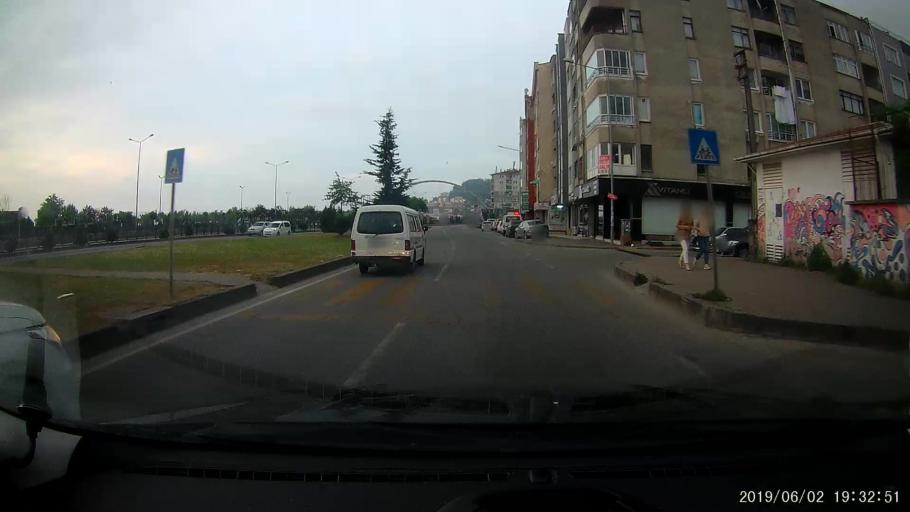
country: TR
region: Giresun
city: Giresun
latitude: 40.9115
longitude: 38.3732
